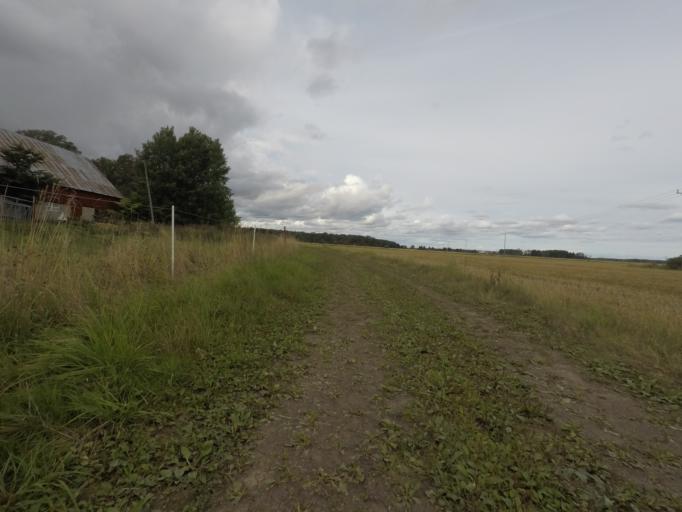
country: SE
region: Vaestmanland
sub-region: Kungsors Kommun
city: Kungsoer
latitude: 59.4563
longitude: 16.0496
